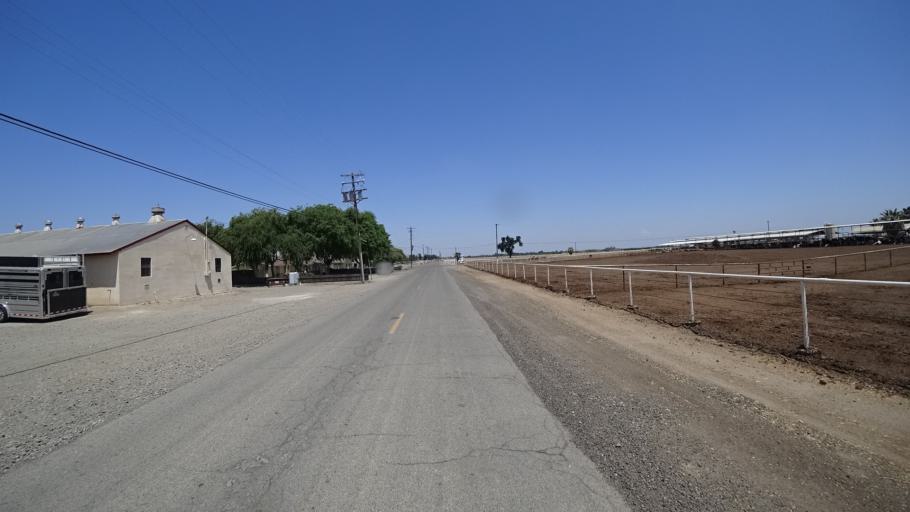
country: US
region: California
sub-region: Kings County
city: Lucerne
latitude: 36.3837
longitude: -119.7270
